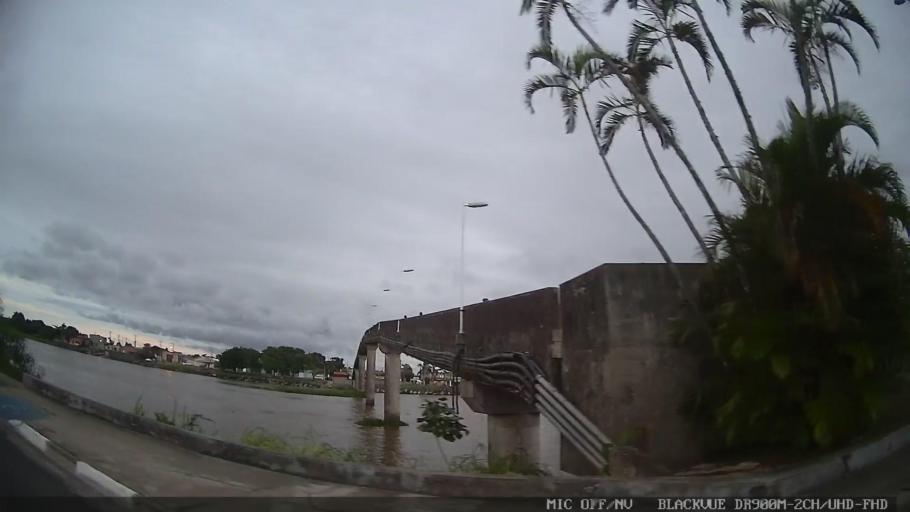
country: BR
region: Sao Paulo
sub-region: Iguape
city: Iguape
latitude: -24.7130
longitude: -47.5621
